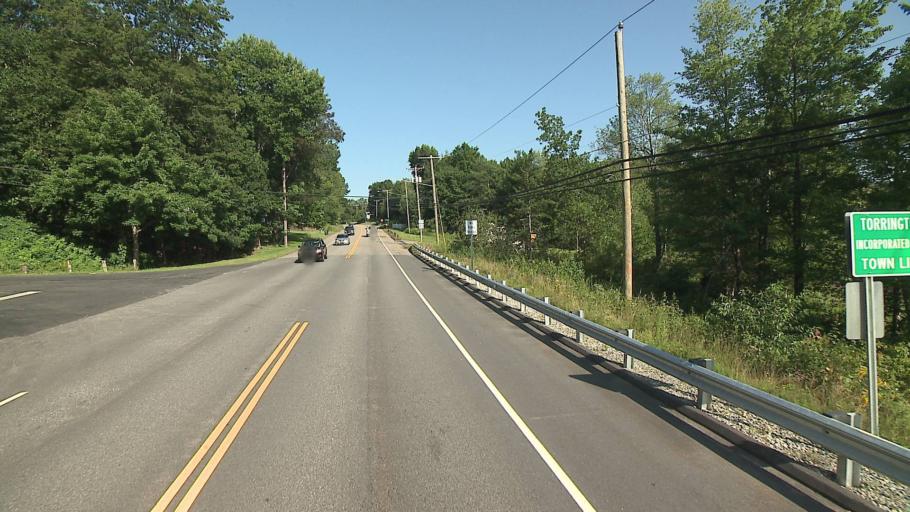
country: US
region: Connecticut
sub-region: Litchfield County
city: Northwest Harwinton
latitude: 41.7984
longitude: -73.0830
